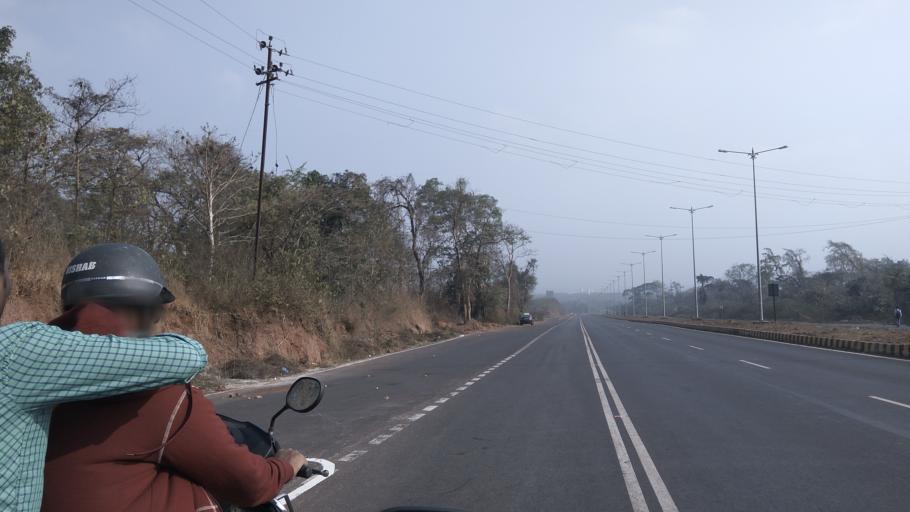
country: IN
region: Goa
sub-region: North Goa
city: Goa Velha
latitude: 15.4912
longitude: 73.9072
